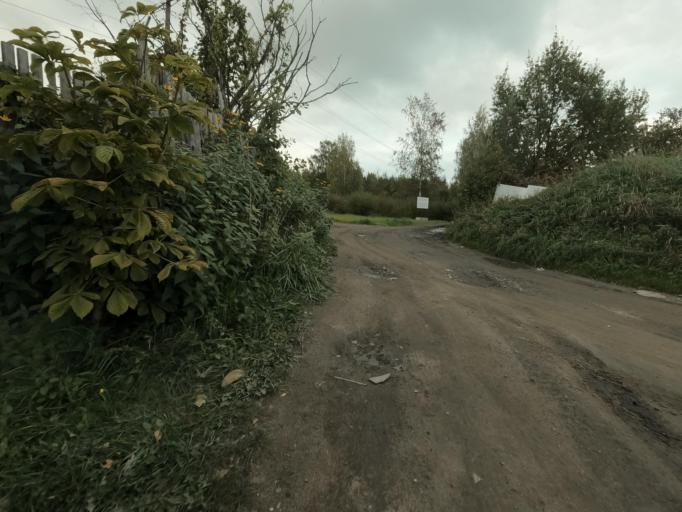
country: RU
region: St.-Petersburg
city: Sapernyy
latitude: 59.7751
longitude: 30.6483
